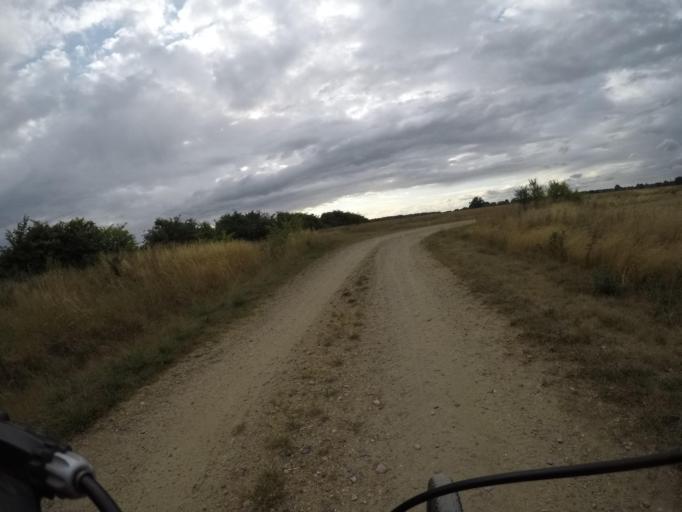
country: DE
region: Lower Saxony
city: Neu Darchau
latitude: 53.2668
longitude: 10.9355
